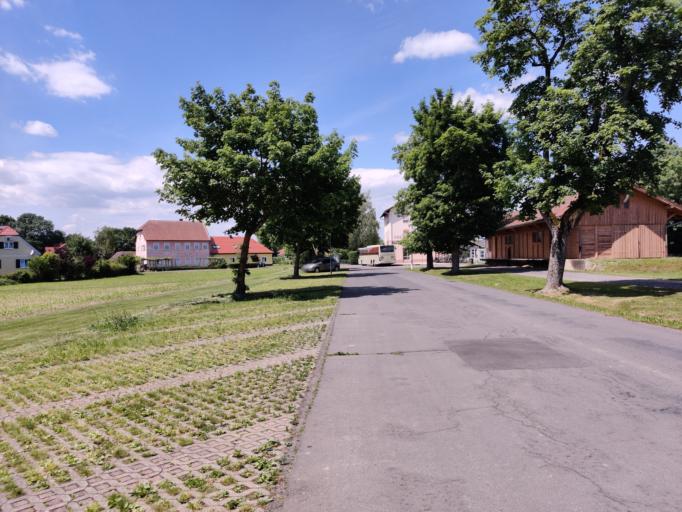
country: AT
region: Styria
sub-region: Politischer Bezirk Suedoststeiermark
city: Bad Radkersburg
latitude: 46.6986
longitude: 15.9936
